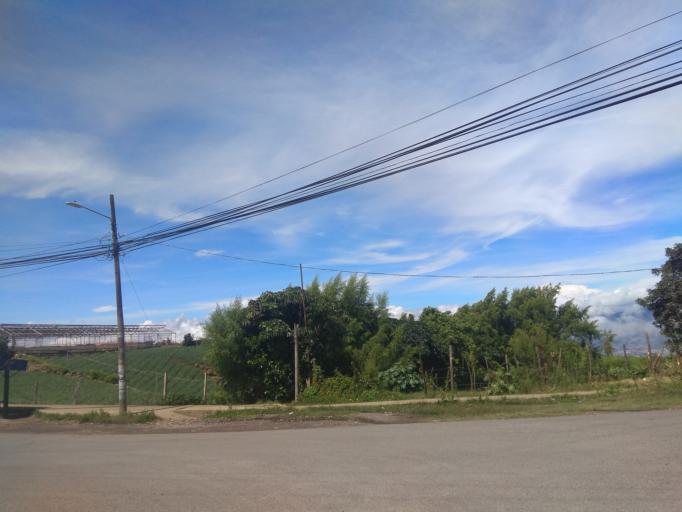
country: CR
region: Cartago
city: Cot
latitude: 9.9149
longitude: -83.8906
